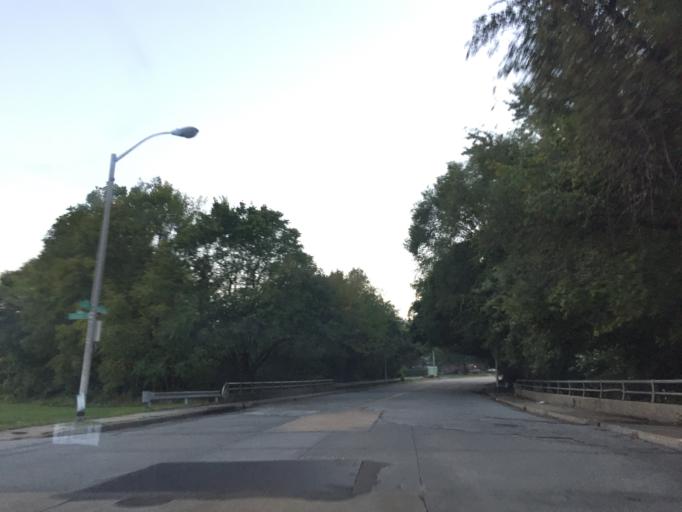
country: US
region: Maryland
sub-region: Baltimore County
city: Rosedale
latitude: 39.3282
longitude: -76.5336
